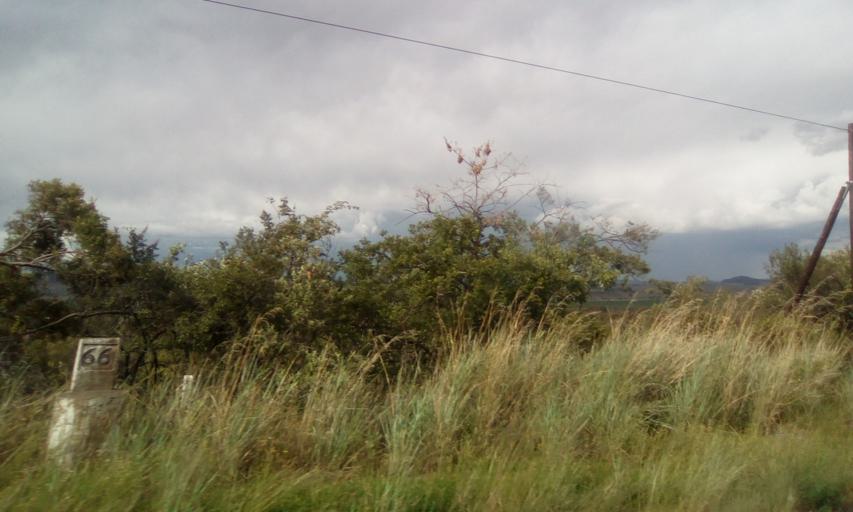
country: ZA
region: Orange Free State
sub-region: Thabo Mofutsanyana District Municipality
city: Ladybrand
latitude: -29.2125
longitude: 27.4599
